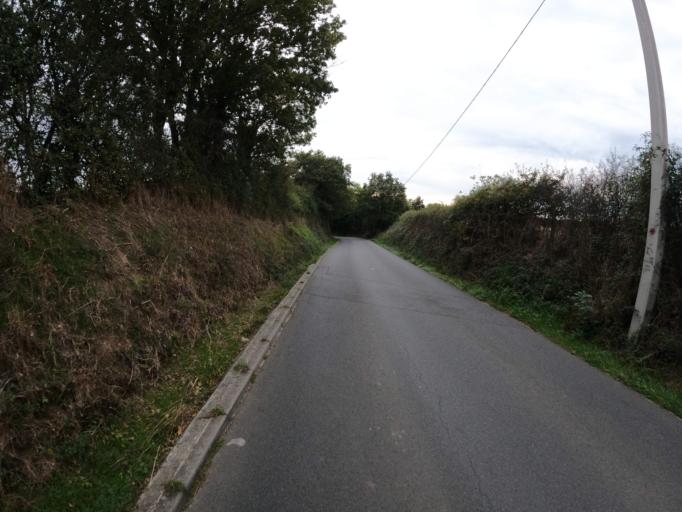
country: FR
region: Pays de la Loire
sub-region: Departement de Maine-et-Loire
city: Saint-Christophe-du-Bois
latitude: 47.0367
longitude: -0.9366
